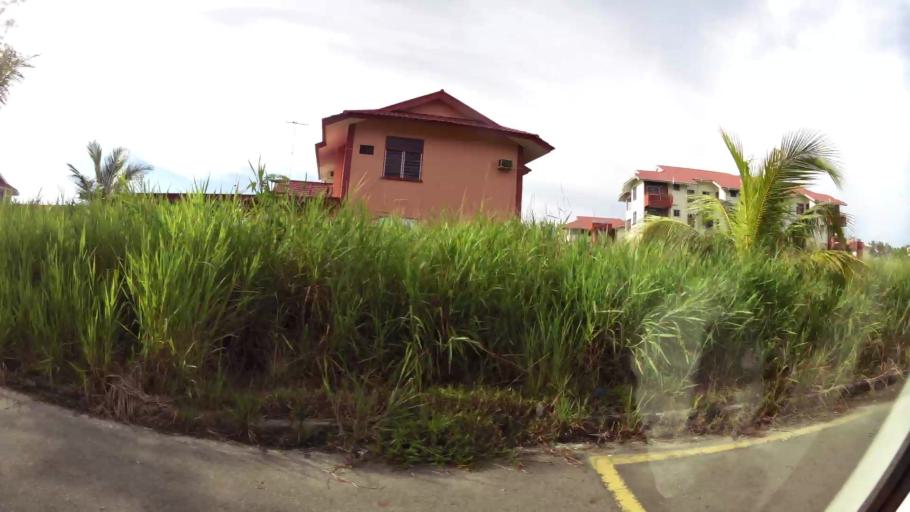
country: BN
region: Brunei and Muara
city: Bandar Seri Begawan
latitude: 4.9733
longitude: 115.0288
